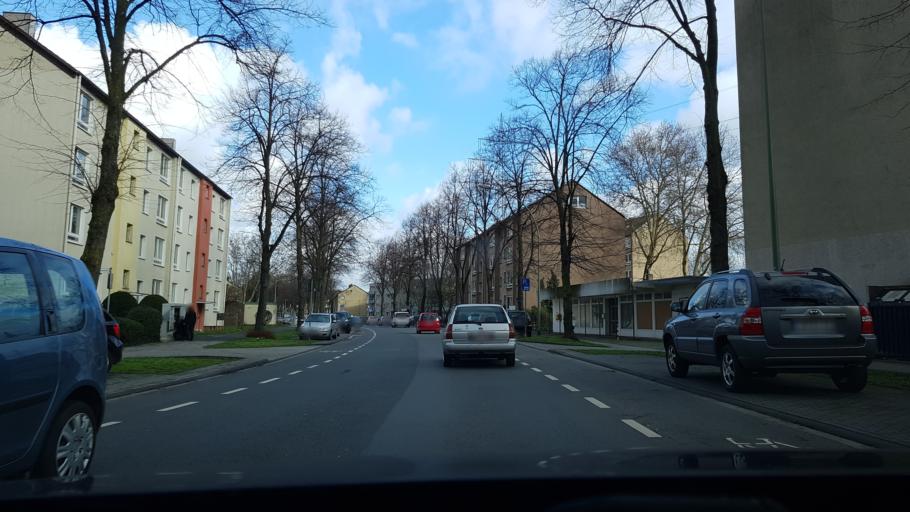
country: DE
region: North Rhine-Westphalia
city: Meiderich
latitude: 51.5072
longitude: 6.7858
